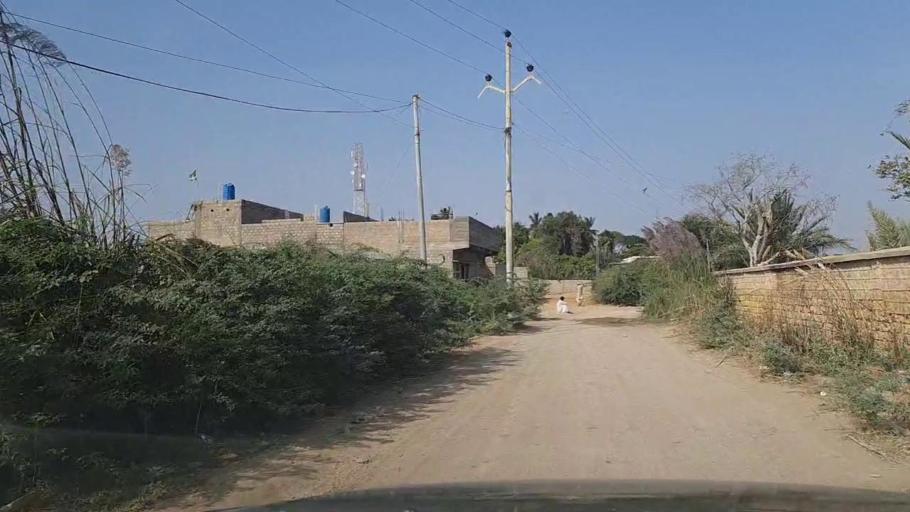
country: PK
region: Sindh
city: Gharo
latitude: 24.7450
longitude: 67.5824
